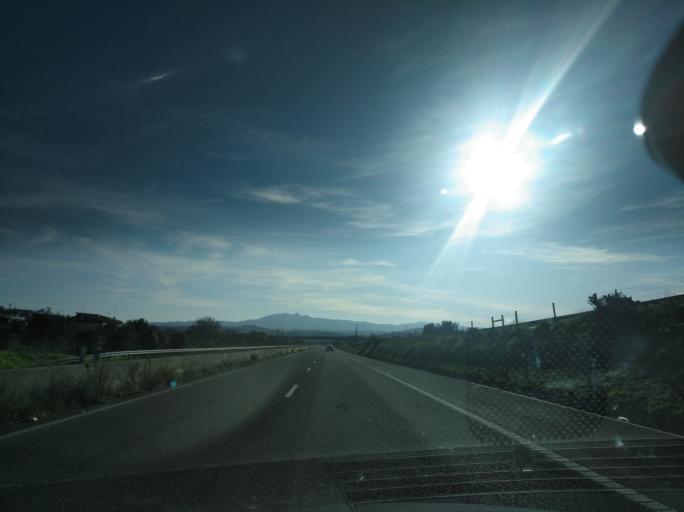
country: PT
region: Lisbon
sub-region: Sintra
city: Pero Pinheiro
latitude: 38.8674
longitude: -9.3346
